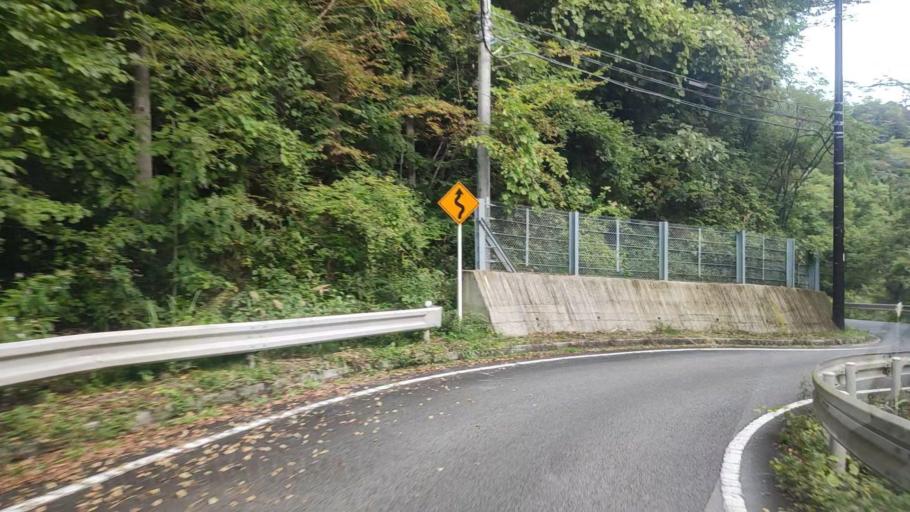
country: JP
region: Gunma
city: Nakanojomachi
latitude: 36.6505
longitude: 138.6397
